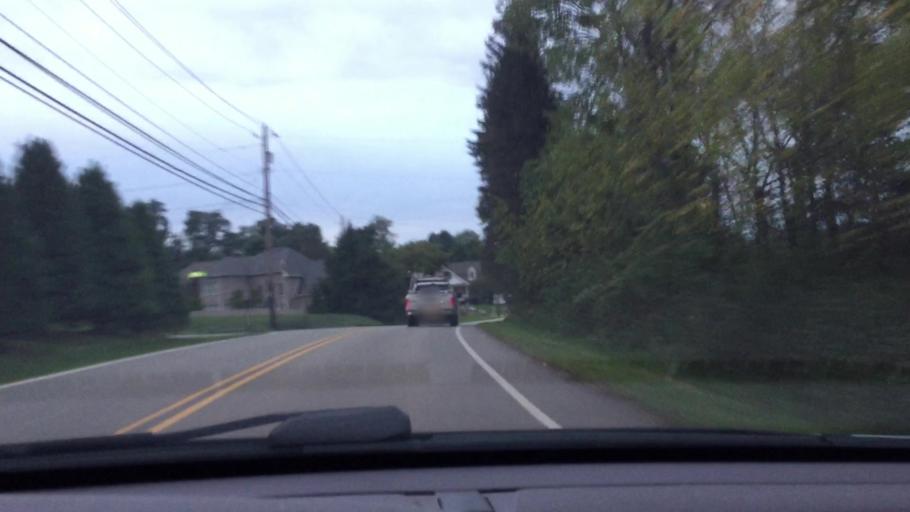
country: US
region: Pennsylvania
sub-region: Westmoreland County
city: Fellsburg
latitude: 40.1914
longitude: -79.7961
